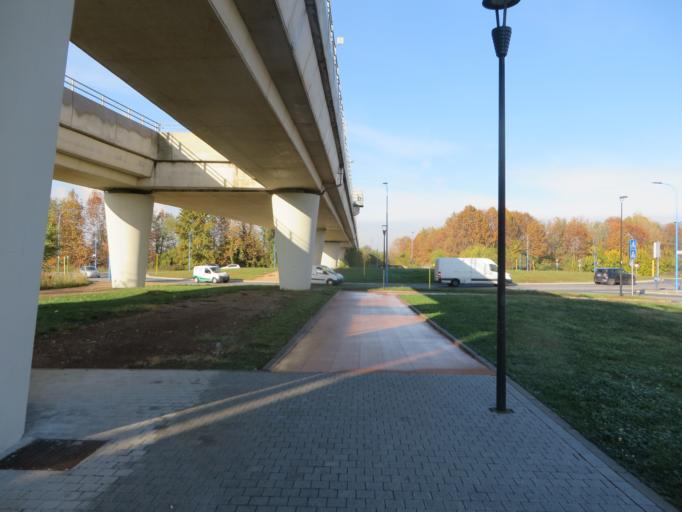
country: IT
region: Lombardy
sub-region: Provincia di Brescia
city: Buffalora-Bettole
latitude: 45.5115
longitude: 10.2796
